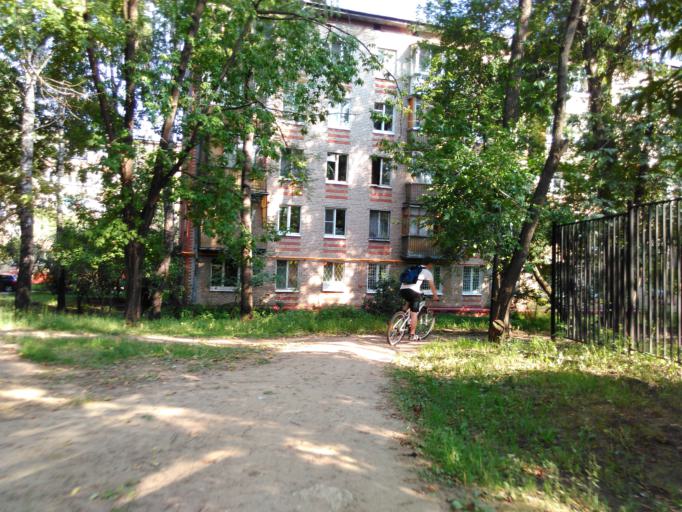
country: RU
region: Moscow
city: Amin'yevo
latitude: 55.7128
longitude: 37.4574
